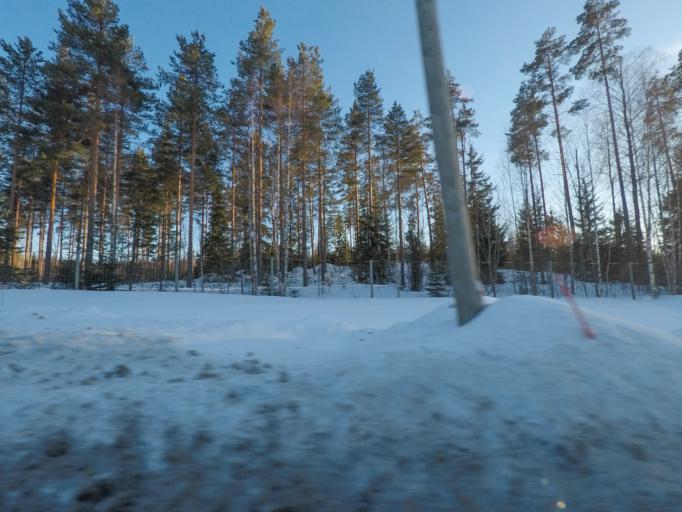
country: FI
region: Southern Savonia
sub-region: Mikkeli
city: Pertunmaa
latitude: 61.4178
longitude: 26.4324
